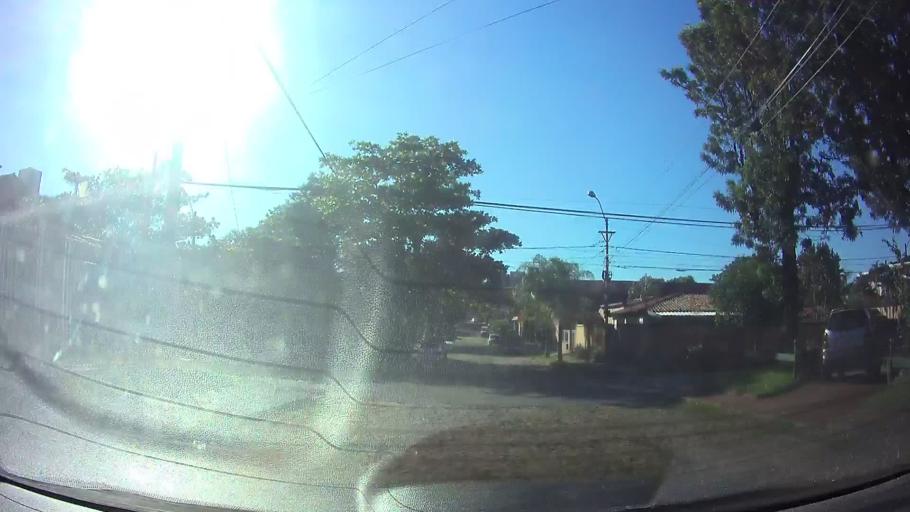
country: PY
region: Central
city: Fernando de la Mora
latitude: -25.2980
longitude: -57.5600
